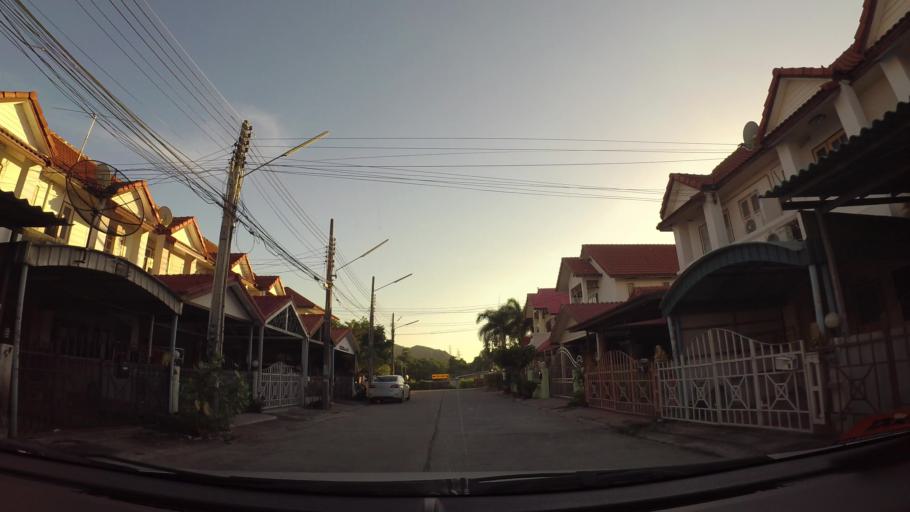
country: TH
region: Chon Buri
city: Si Racha
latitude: 13.1325
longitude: 100.9381
